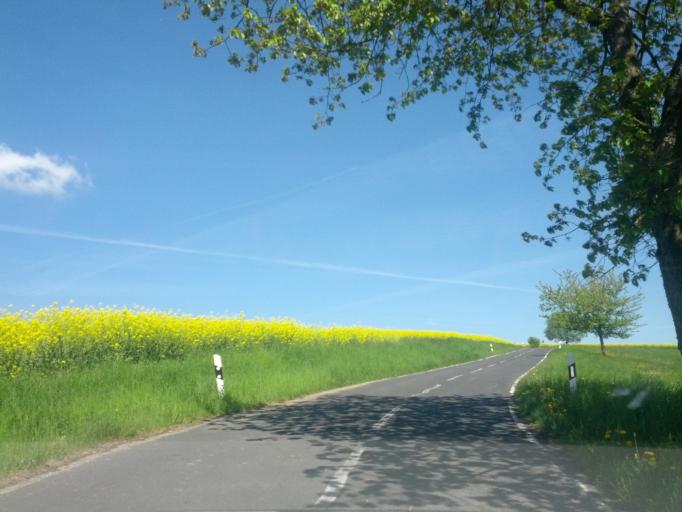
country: DE
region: Thuringia
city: Treffurt
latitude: 51.1070
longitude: 10.2117
